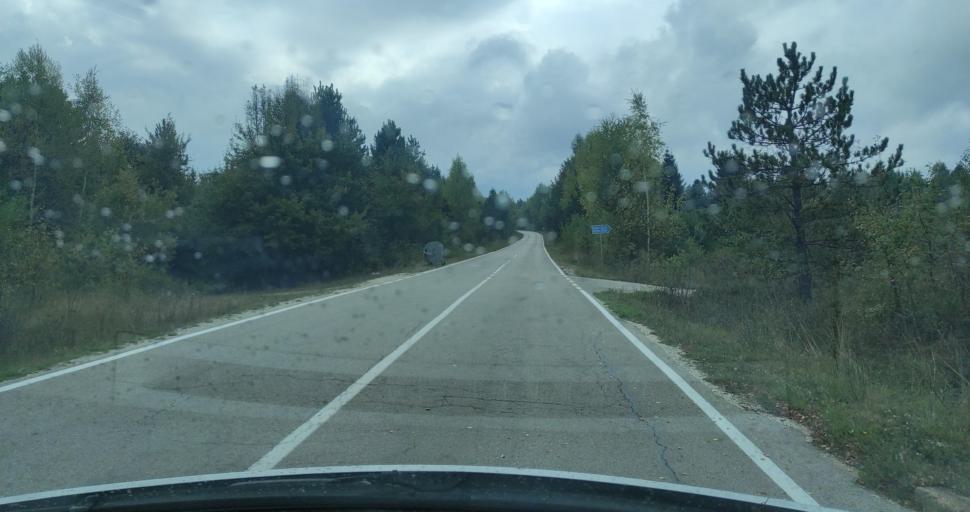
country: RS
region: Central Serbia
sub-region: Jablanicki Okrug
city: Crna Trava
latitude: 42.6869
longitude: 22.3157
